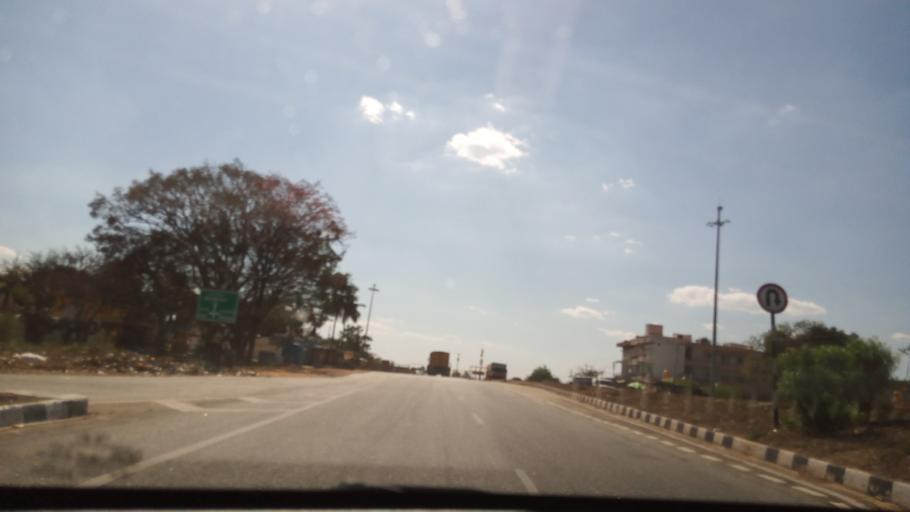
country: IN
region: Karnataka
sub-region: Kolar
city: Mulbagal
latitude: 13.1542
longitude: 78.3320
